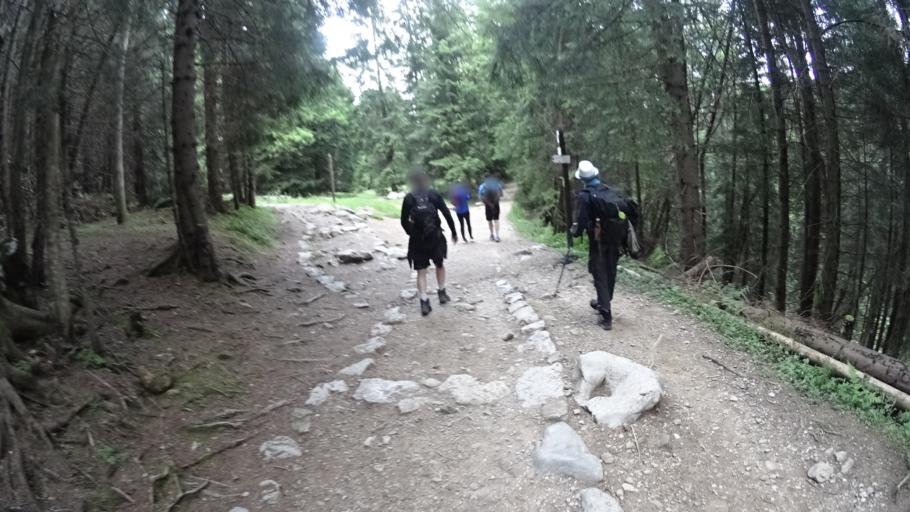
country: PL
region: Lesser Poland Voivodeship
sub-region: Powiat tatrzanski
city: Zakopane
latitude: 49.2559
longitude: 19.9690
